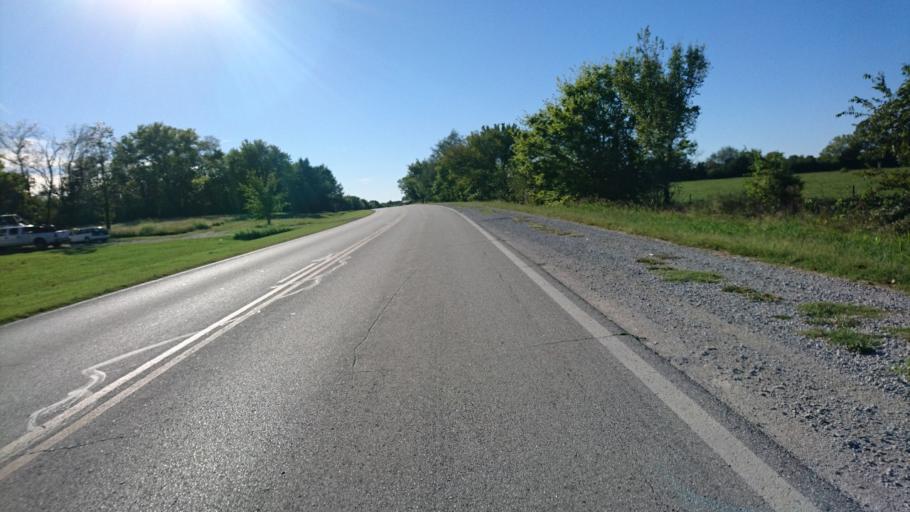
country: US
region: Missouri
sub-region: Jasper County
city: Carthage
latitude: 37.1734
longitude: -94.3658
